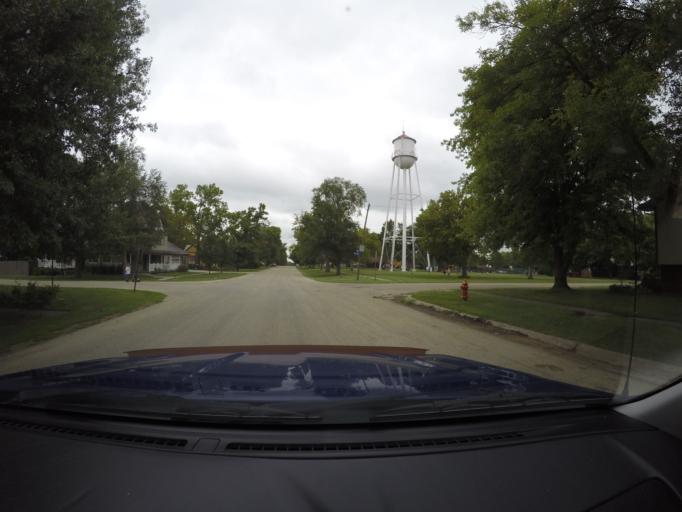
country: US
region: Kansas
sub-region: Morris County
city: Council Grove
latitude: 38.8649
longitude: -96.4885
